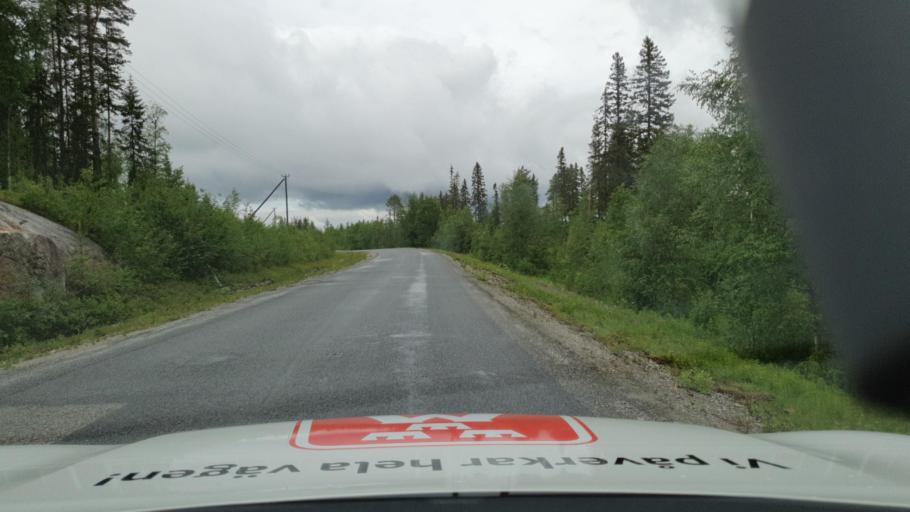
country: SE
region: Vaesterbotten
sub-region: Dorotea Kommun
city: Dorotea
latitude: 64.1772
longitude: 16.6390
